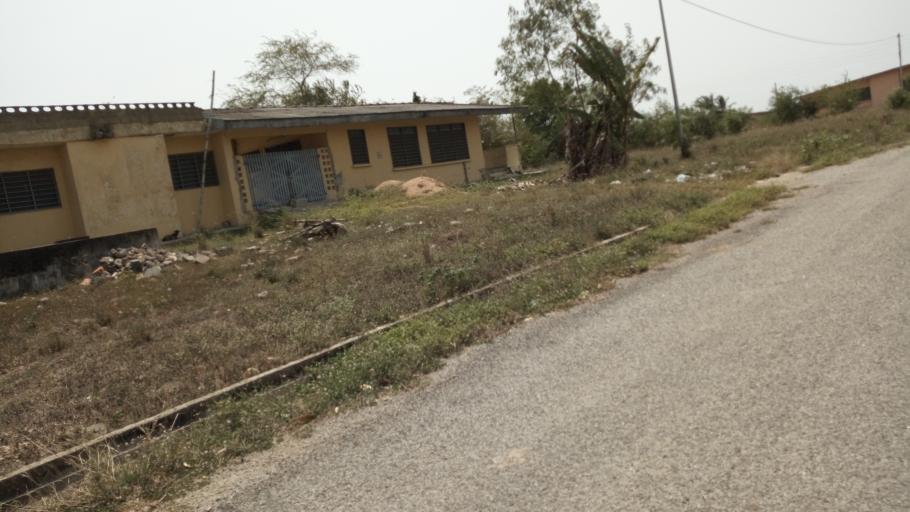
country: GH
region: Central
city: Winneba
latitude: 5.3677
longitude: -0.6462
